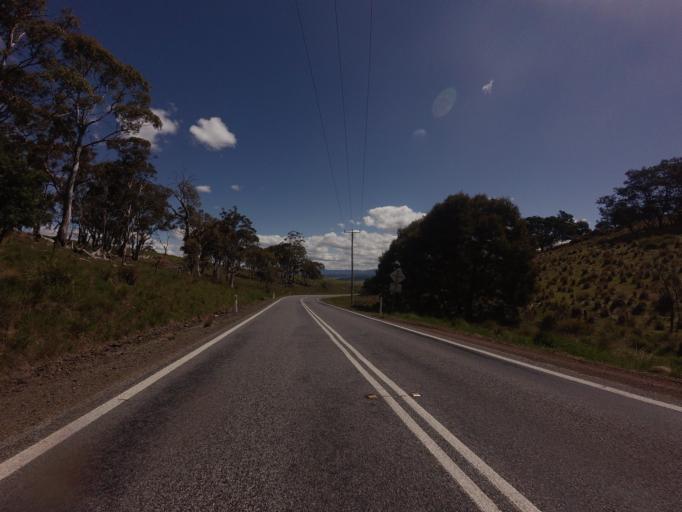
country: AU
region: Tasmania
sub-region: Northern Midlands
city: Evandale
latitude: -41.9409
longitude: 147.5945
